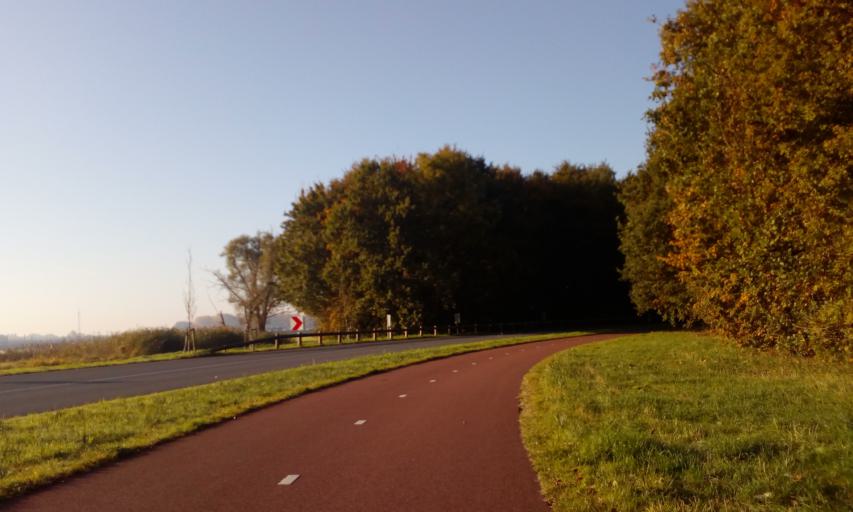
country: NL
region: South Holland
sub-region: Gemeente Lansingerland
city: Berkel en Rodenrijs
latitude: 51.9787
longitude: 4.4679
